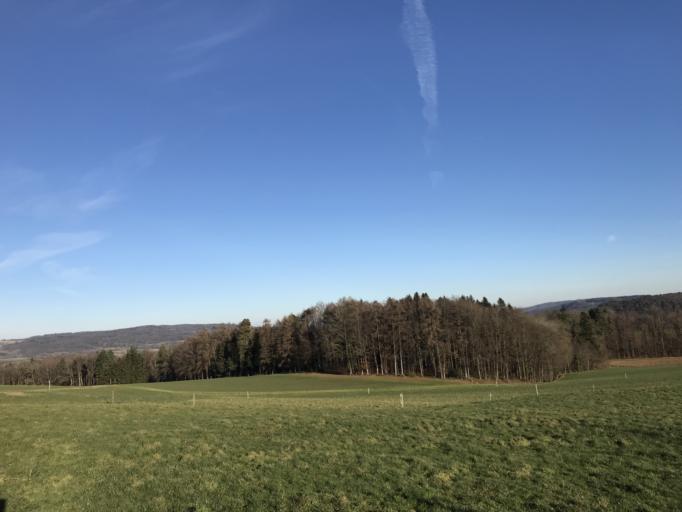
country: CH
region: Thurgau
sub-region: Frauenfeld District
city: Eschenz
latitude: 47.6346
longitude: 8.8552
